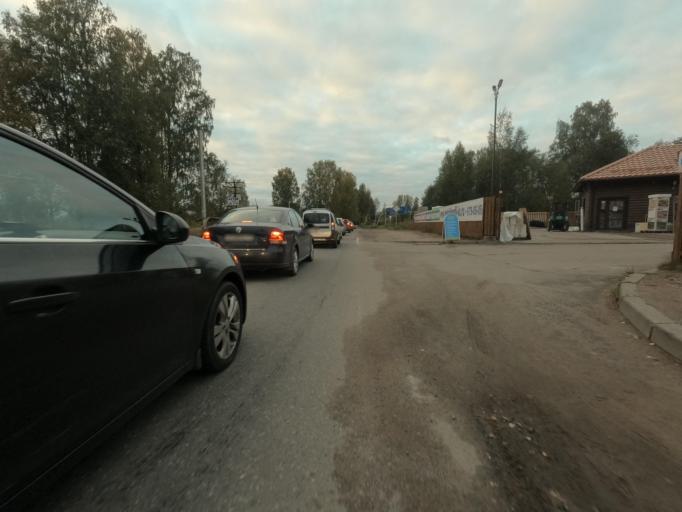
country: RU
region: Leningrad
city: Pavlovo
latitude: 59.8127
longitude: 30.9219
